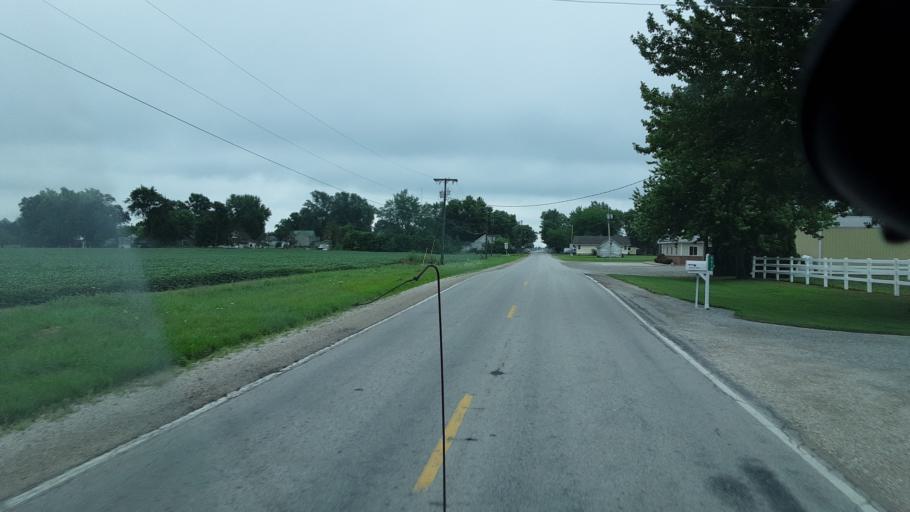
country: US
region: Indiana
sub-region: Wells County
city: Bluffton
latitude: 40.7810
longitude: -85.0908
